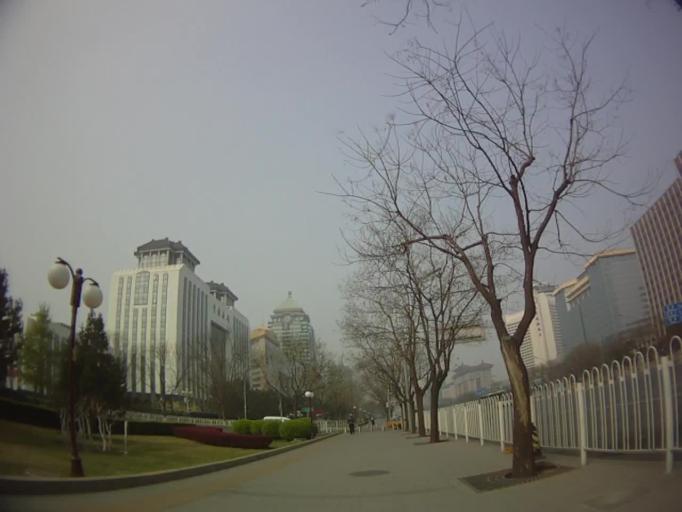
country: CN
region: Beijing
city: Chaowai
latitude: 39.9069
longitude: 116.4272
